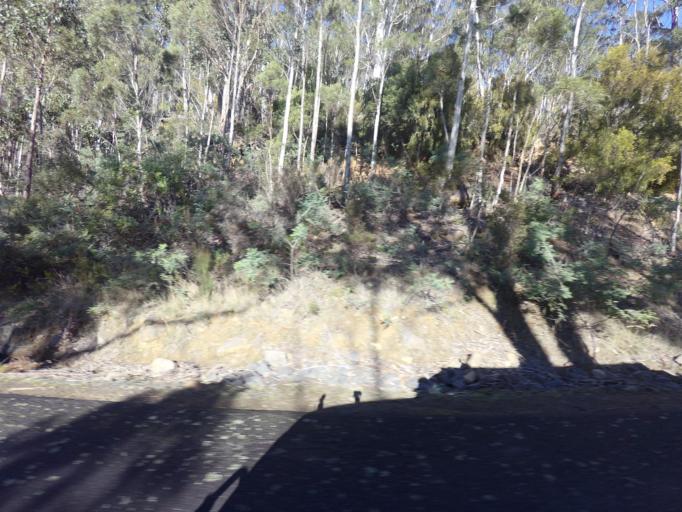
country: AU
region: Tasmania
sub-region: Glenorchy
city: Berriedale
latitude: -42.8367
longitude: 147.1673
